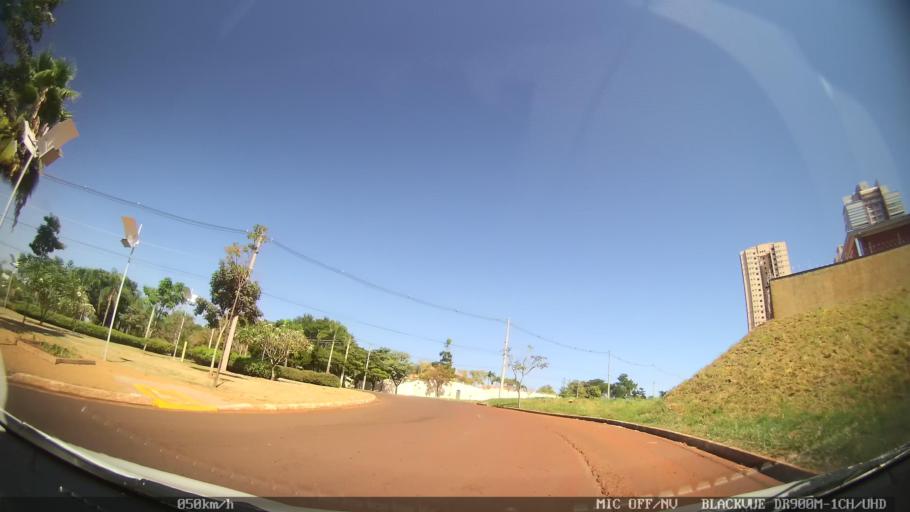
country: BR
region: Sao Paulo
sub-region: Ribeirao Preto
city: Ribeirao Preto
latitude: -21.2189
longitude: -47.8014
